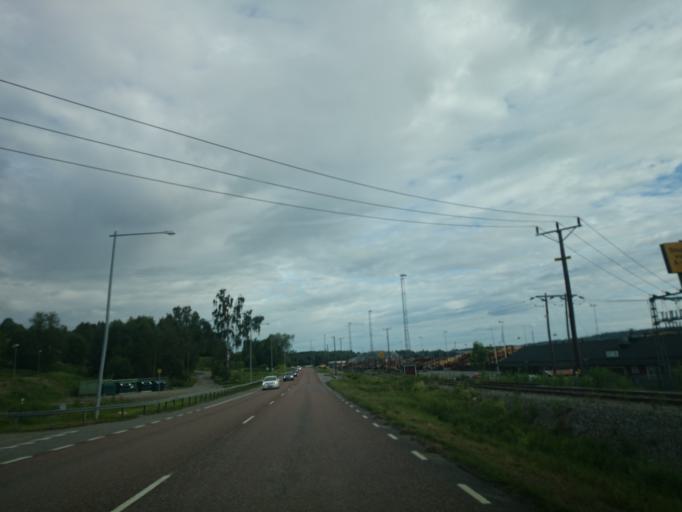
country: SE
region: Vaesternorrland
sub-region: Sundsvalls Kommun
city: Johannedal
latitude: 62.4171
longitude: 17.3825
